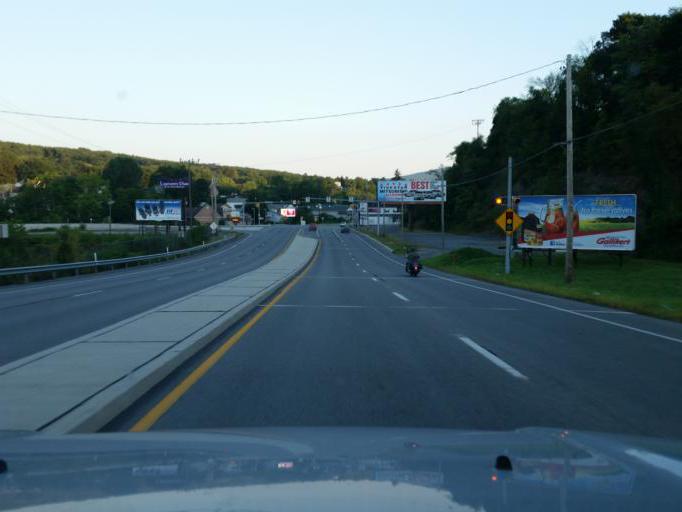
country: US
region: Pennsylvania
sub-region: Blair County
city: Lakemont
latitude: 40.4679
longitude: -78.3975
